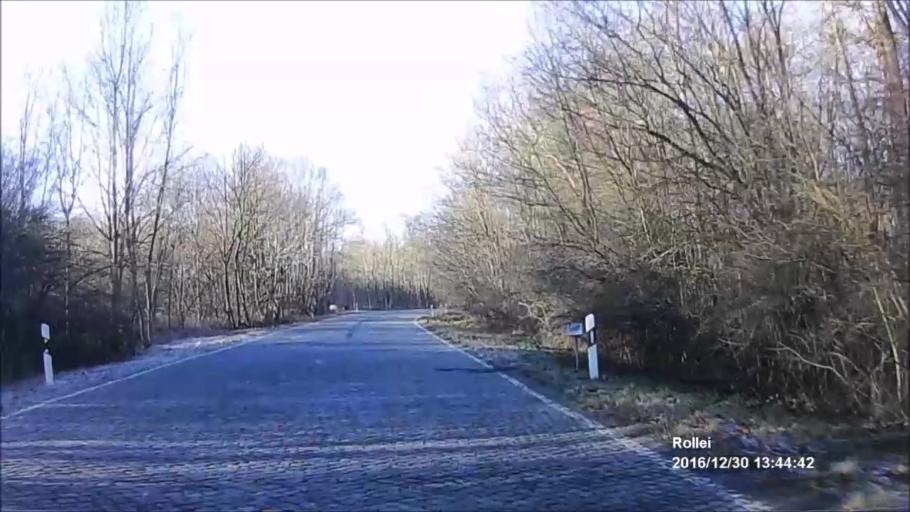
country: DE
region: Thuringia
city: Rockhausen
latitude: 50.9208
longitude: 11.0785
